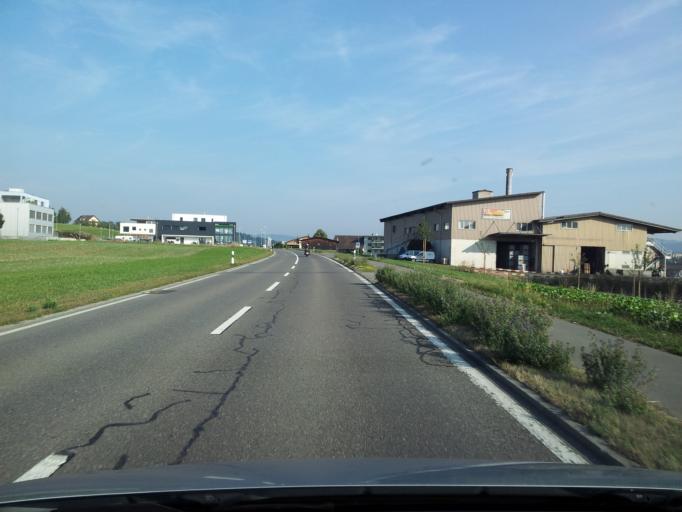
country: CH
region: Lucerne
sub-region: Sursee District
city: Oberkirch
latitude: 47.1496
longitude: 8.1188
